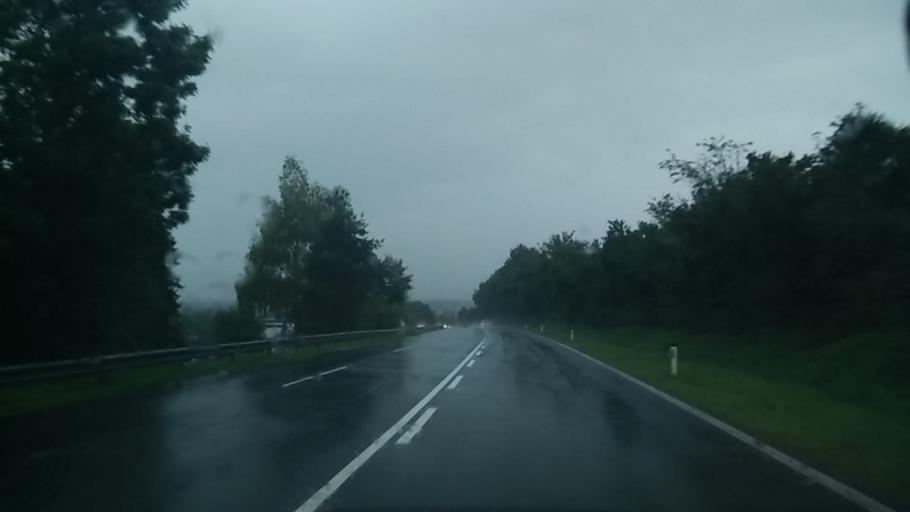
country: AT
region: Carinthia
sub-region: Politischer Bezirk Villach Land
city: Wernberg
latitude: 46.6254
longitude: 13.9276
